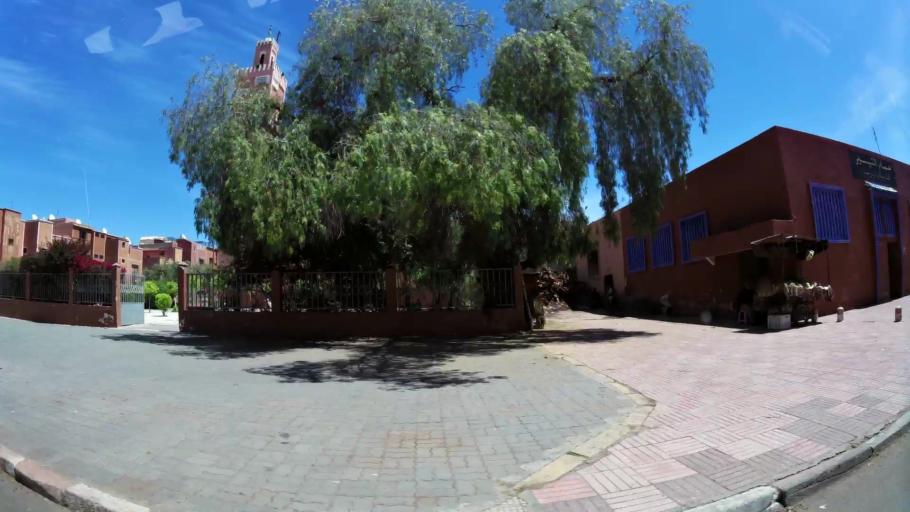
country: MA
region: Marrakech-Tensift-Al Haouz
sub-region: Marrakech
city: Marrakesh
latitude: 31.6330
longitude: -8.0471
